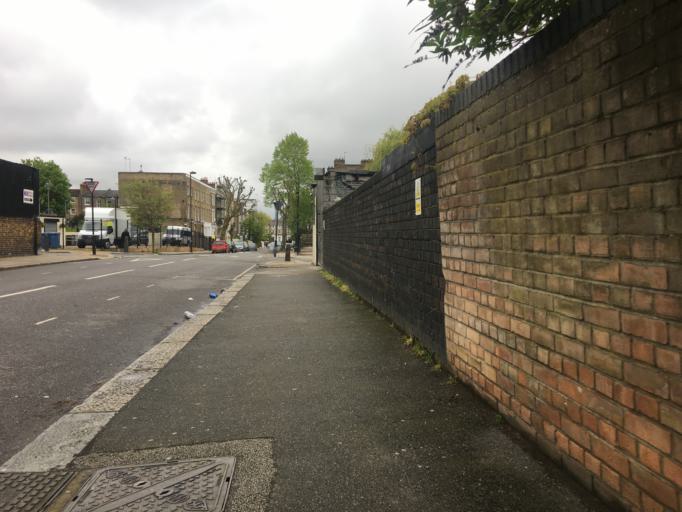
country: GB
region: England
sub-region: Greater London
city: Camden Town
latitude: 51.5480
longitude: -0.1352
